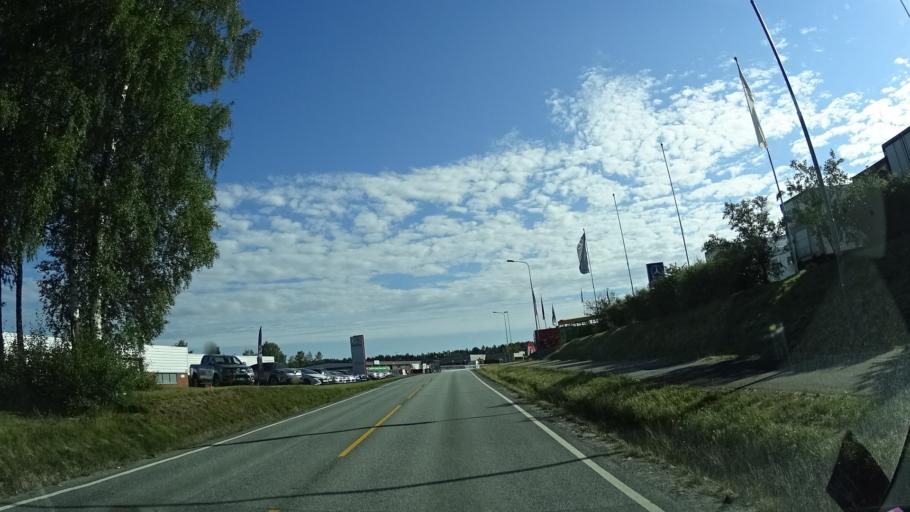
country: NO
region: Ostfold
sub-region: Eidsberg
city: Mysen
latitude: 59.5532
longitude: 11.3648
